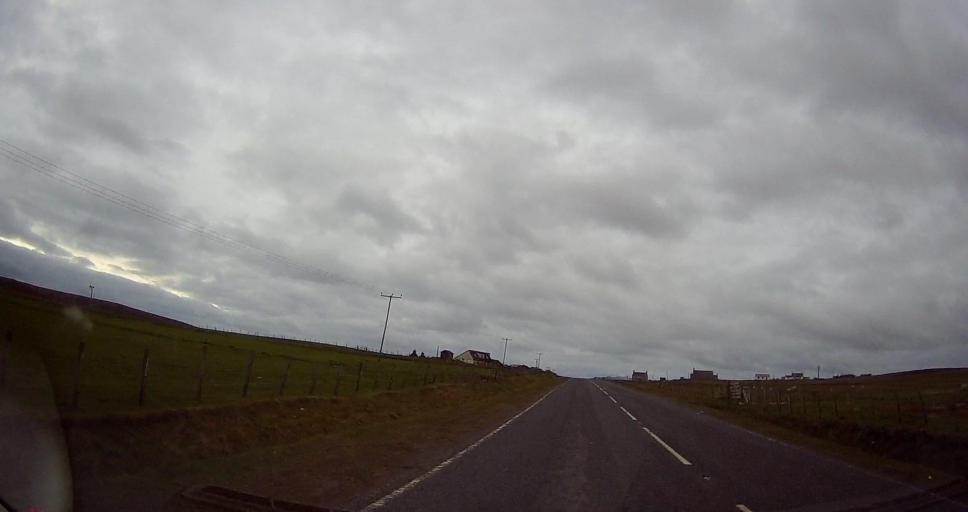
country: GB
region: Scotland
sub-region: Shetland Islands
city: Shetland
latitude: 60.6622
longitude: -1.0519
